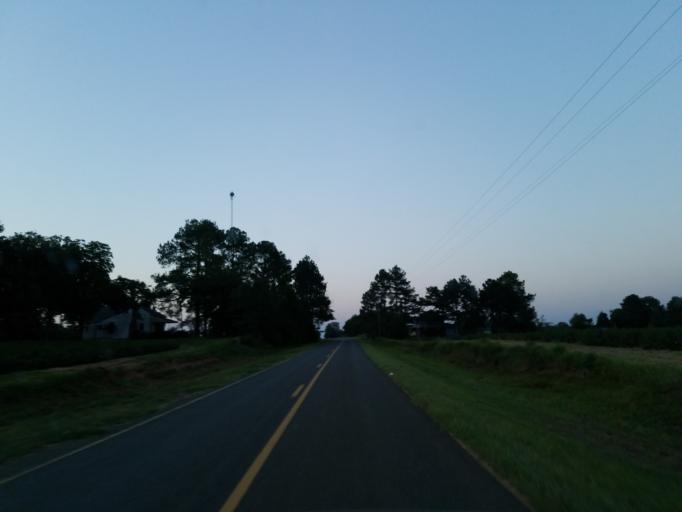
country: US
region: Georgia
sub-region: Dooly County
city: Unadilla
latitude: 32.2381
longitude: -83.7975
